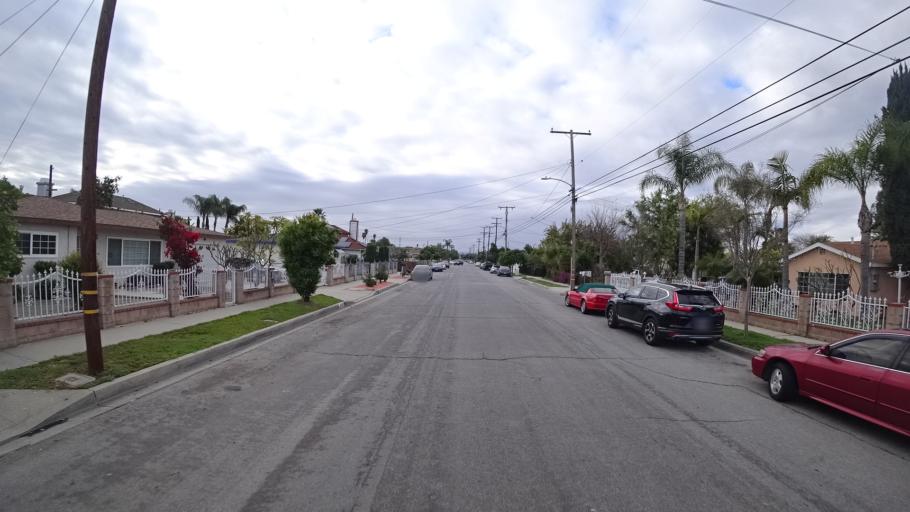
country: US
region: California
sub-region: Los Angeles County
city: Baldwin Park
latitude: 34.0955
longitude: -117.9715
